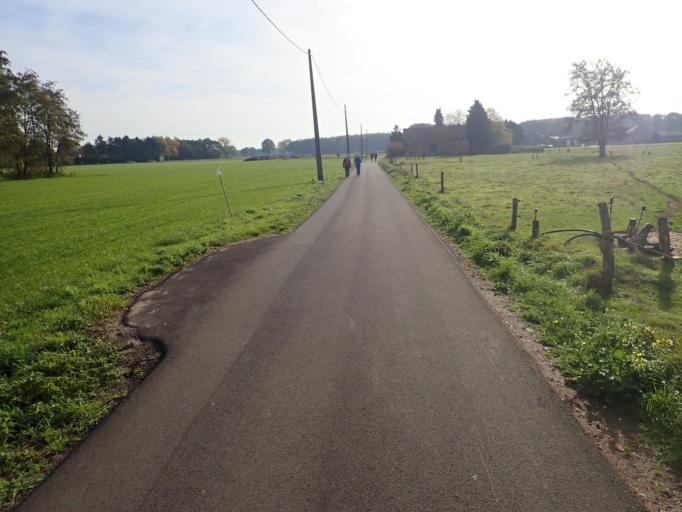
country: BE
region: Flanders
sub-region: Provincie Antwerpen
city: Zoersel
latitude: 51.2652
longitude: 4.7209
